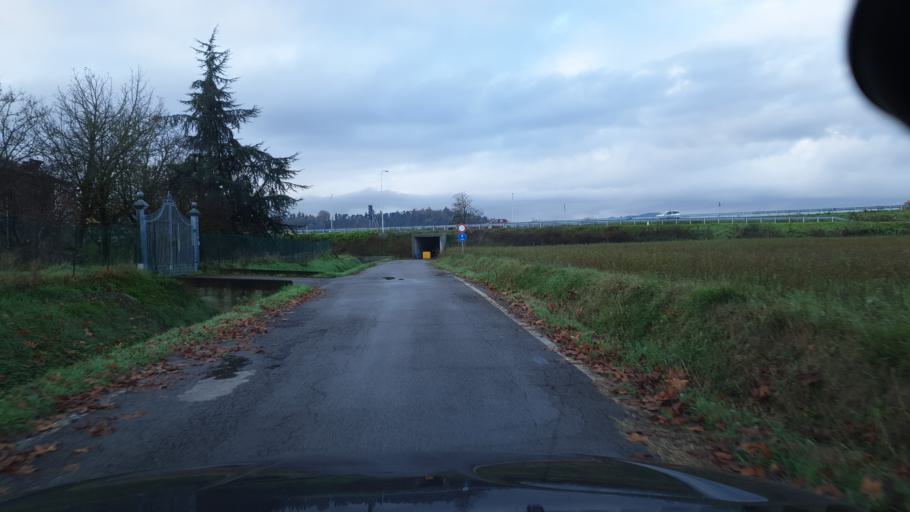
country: IT
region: Emilia-Romagna
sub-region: Provincia di Bologna
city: Crespellano
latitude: 44.5194
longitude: 11.1427
